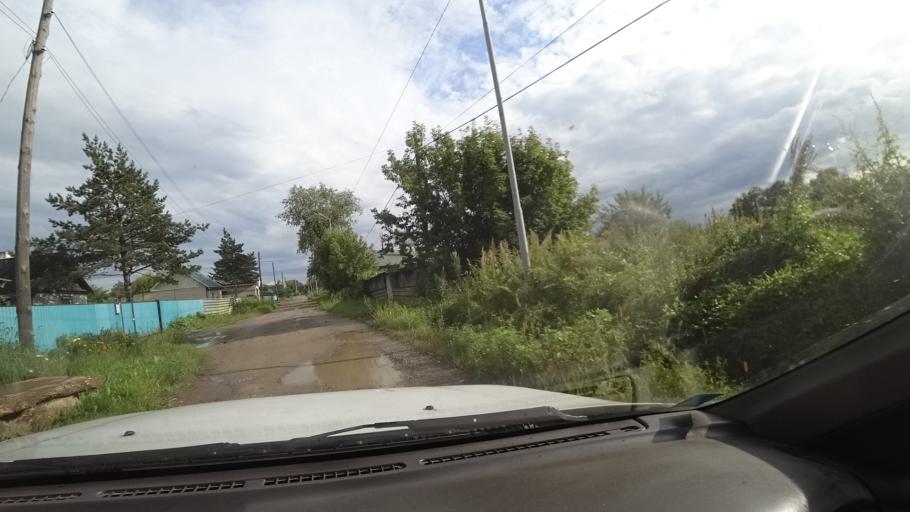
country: RU
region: Primorskiy
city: Dal'nerechensk
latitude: 45.9337
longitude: 133.7474
